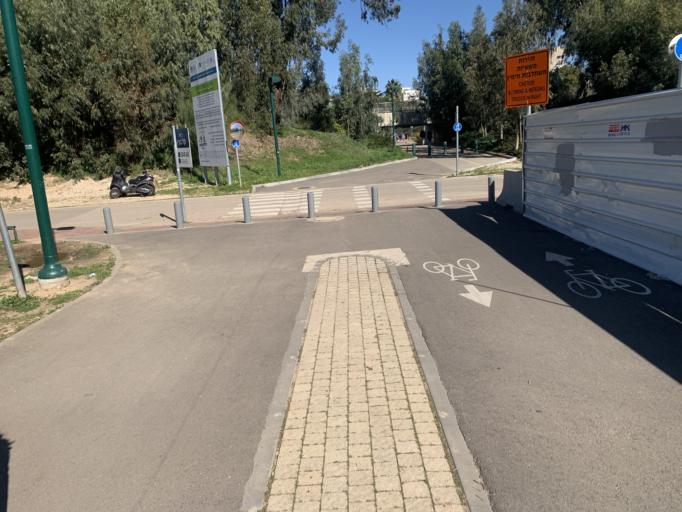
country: IL
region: Tel Aviv
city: Ramat Gan
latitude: 32.1033
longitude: 34.8200
